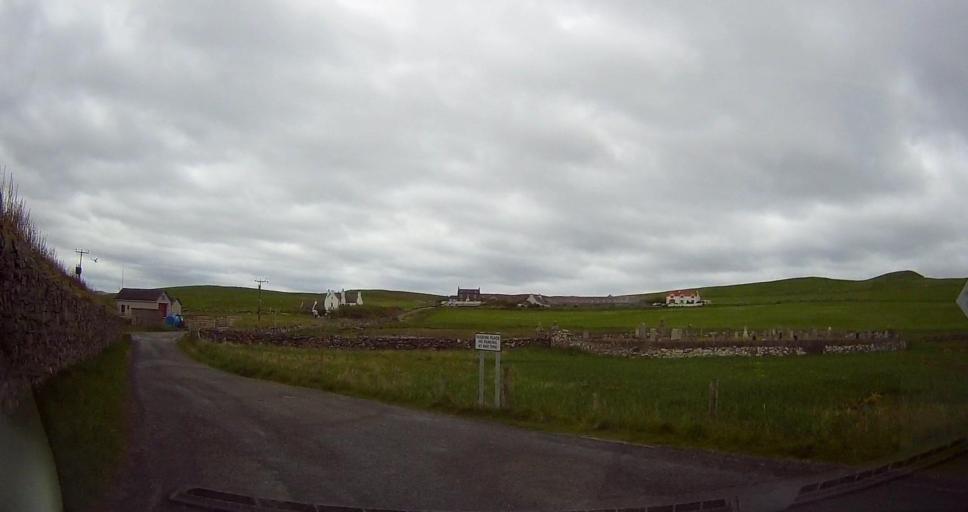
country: GB
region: Scotland
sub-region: Shetland Islands
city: Lerwick
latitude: 60.4763
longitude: -1.4898
